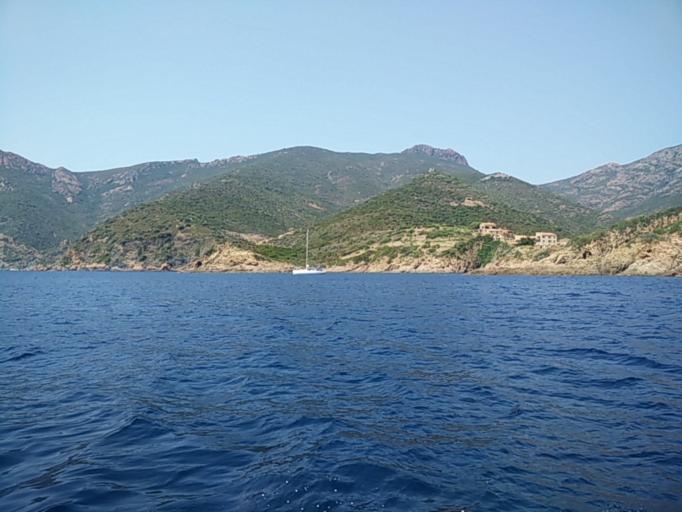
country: FR
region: Corsica
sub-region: Departement de la Corse-du-Sud
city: Cargese
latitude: 42.3452
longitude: 8.6116
